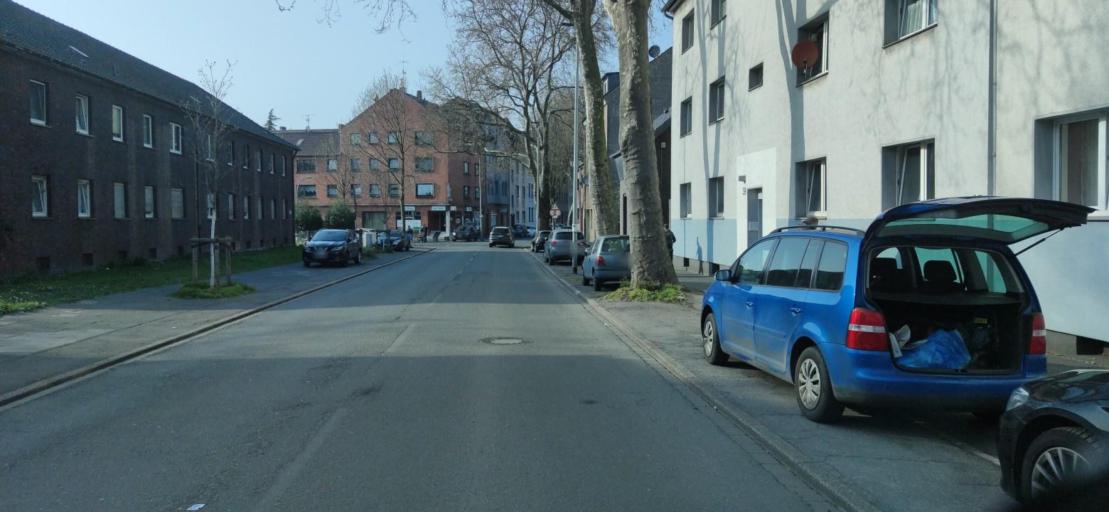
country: DE
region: North Rhine-Westphalia
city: Meiderich
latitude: 51.4612
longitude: 6.7764
